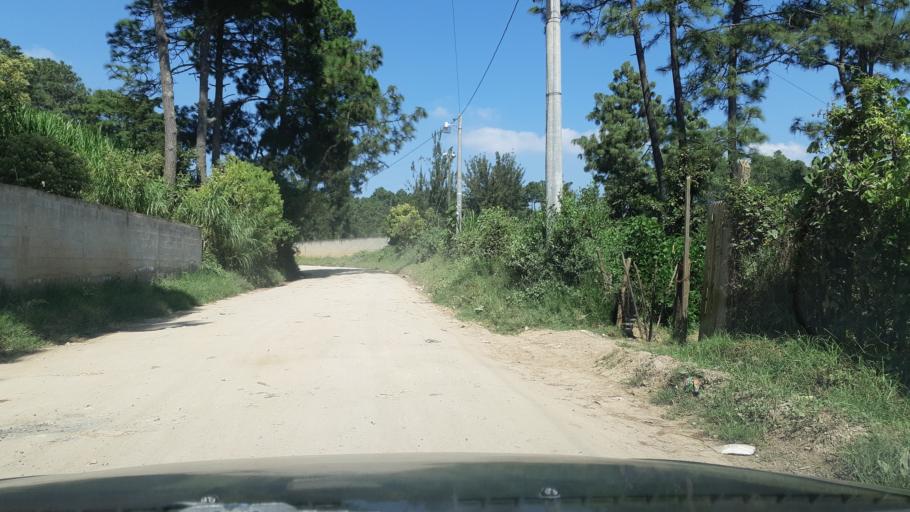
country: GT
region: Chimaltenango
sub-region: Municipio de Chimaltenango
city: Chimaltenango
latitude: 14.6679
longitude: -90.8350
